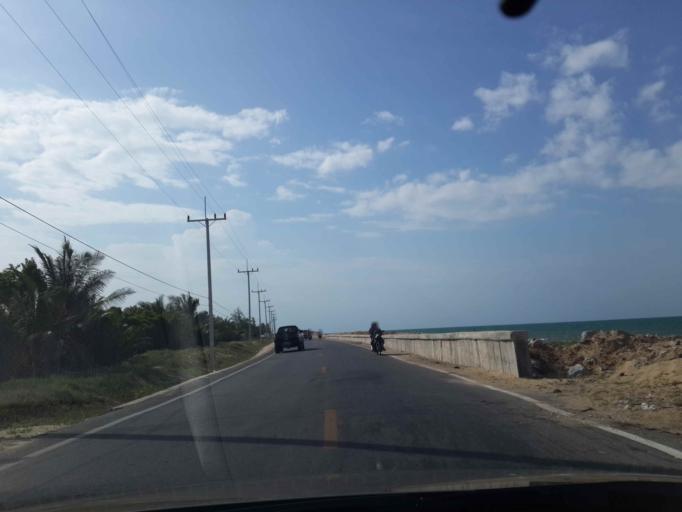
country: TH
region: Pattani
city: Yaring
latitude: 6.9236
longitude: 101.3294
